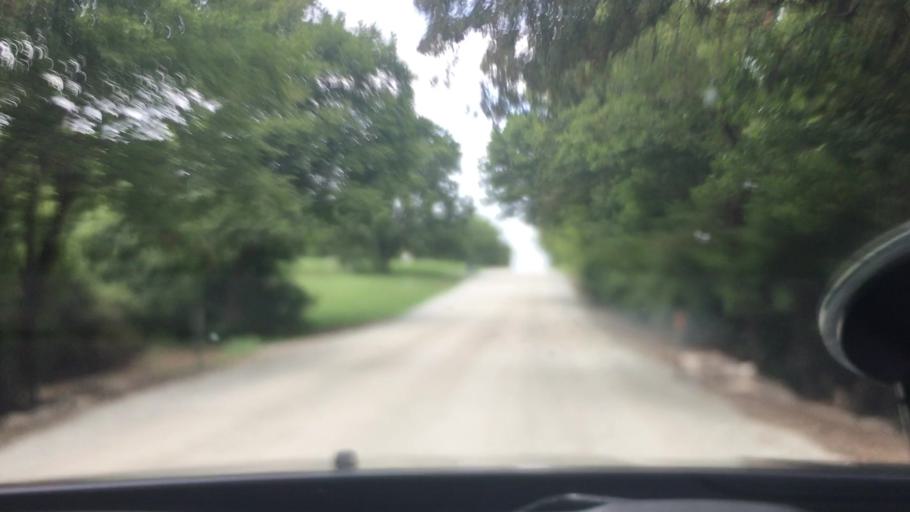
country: US
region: Oklahoma
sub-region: Pontotoc County
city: Ada
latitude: 34.8203
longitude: -96.7572
